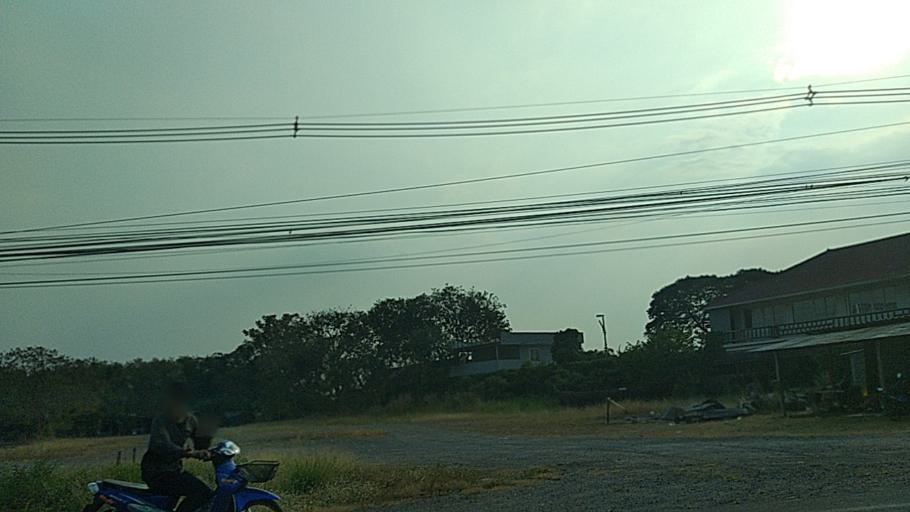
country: TH
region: Nakhon Nayok
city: Nakhon Nayok
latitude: 14.2091
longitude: 101.1809
